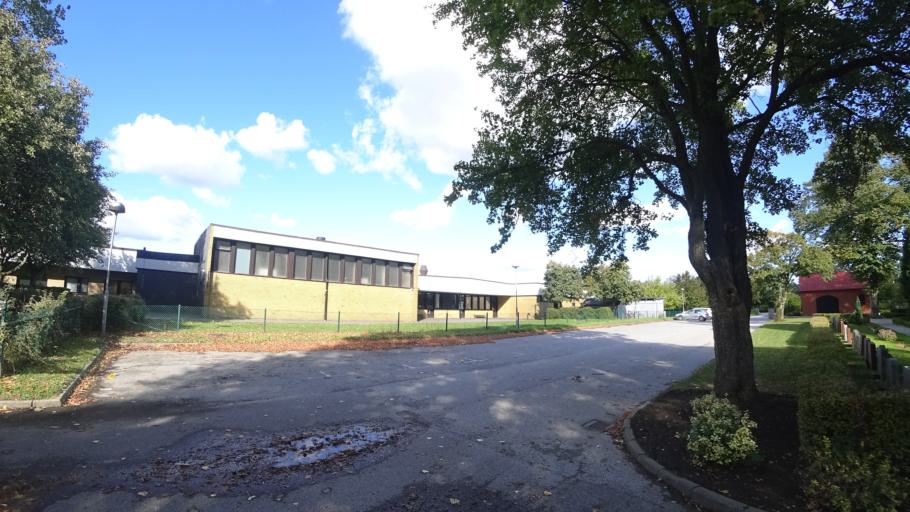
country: SE
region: Skane
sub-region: Kavlinge Kommun
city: Kaevlinge
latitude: 55.7928
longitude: 13.1045
